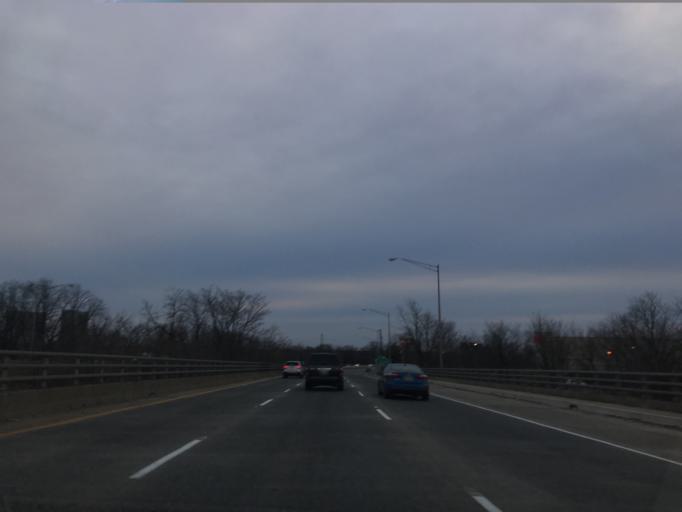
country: US
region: New Jersey
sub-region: Middlesex County
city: Highland Park
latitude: 40.4909
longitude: -74.4136
